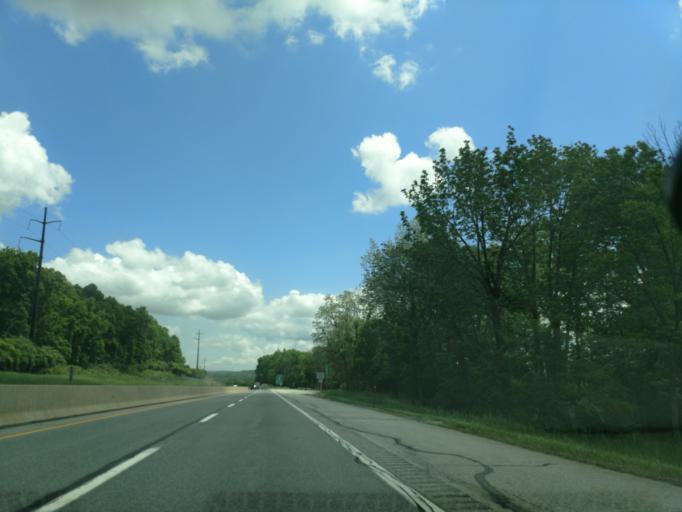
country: US
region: Pennsylvania
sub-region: Lancaster County
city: Reamstown
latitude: 40.2289
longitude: -76.1177
